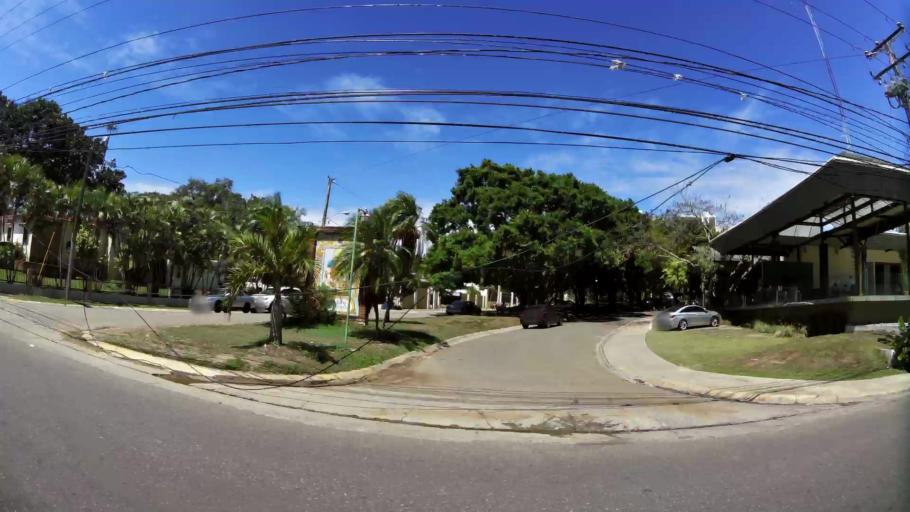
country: DO
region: Santiago
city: Santiago de los Caballeros
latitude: 19.4531
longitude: -70.6920
